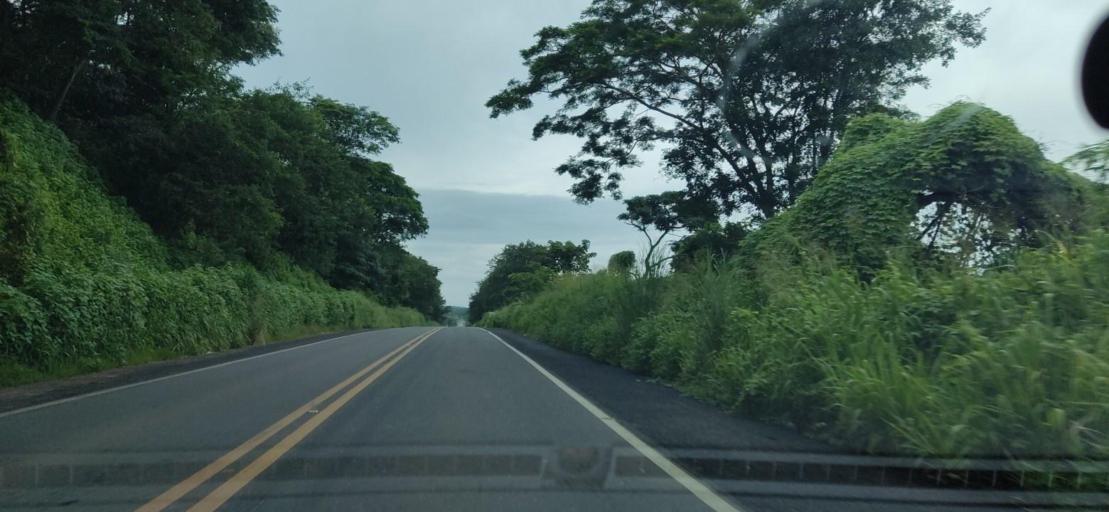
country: BR
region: Piaui
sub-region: Elesbao Veloso
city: Elesbao Veloso
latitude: -6.1930
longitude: -42.1169
